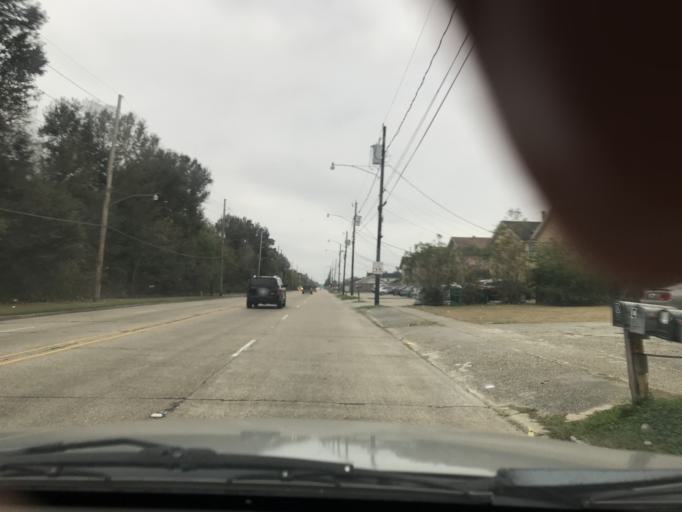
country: US
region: Louisiana
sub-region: Jefferson Parish
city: Woodmere
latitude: 29.8659
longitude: -90.0744
